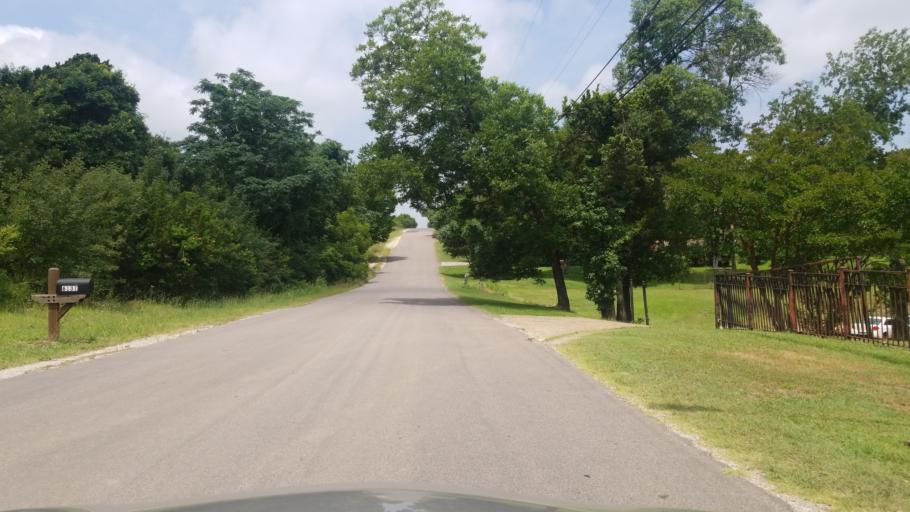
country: US
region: Texas
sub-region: Dallas County
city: Duncanville
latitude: 32.6765
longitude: -96.9274
